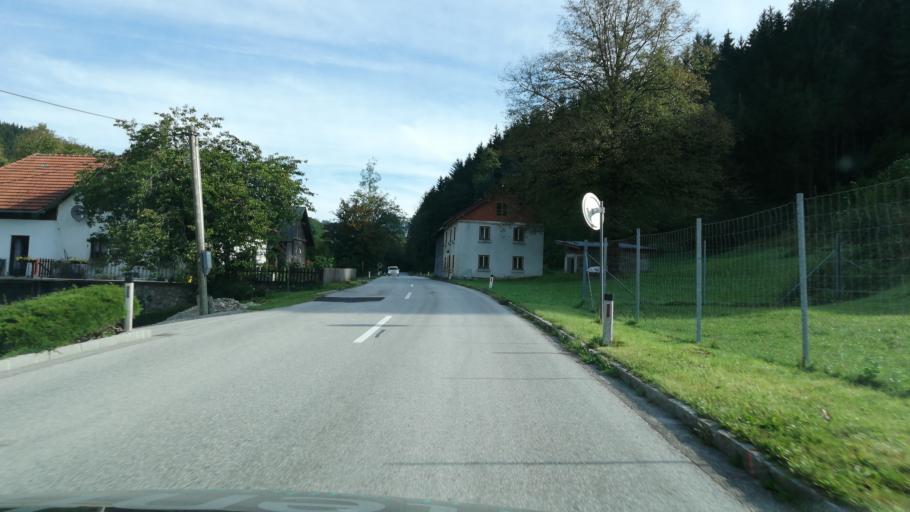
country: AT
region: Upper Austria
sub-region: Politischer Bezirk Steyr-Land
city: Maria Neustift
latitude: 47.9199
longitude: 14.5858
